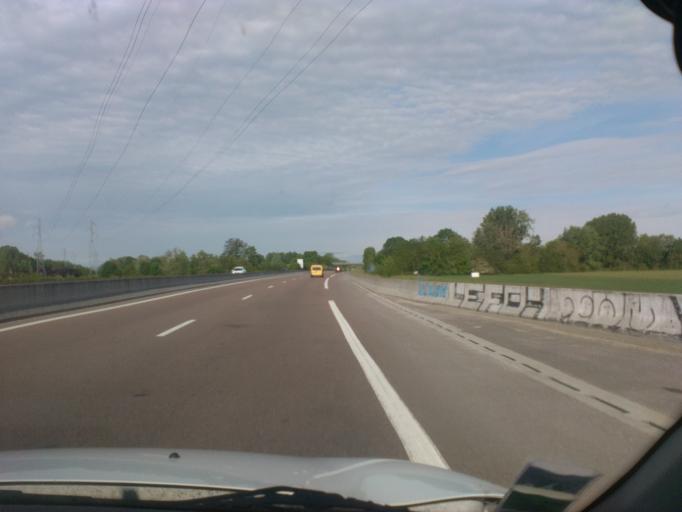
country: FR
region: Champagne-Ardenne
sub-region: Departement de l'Aube
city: Pont-Sainte-Marie
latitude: 48.3276
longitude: 4.0734
